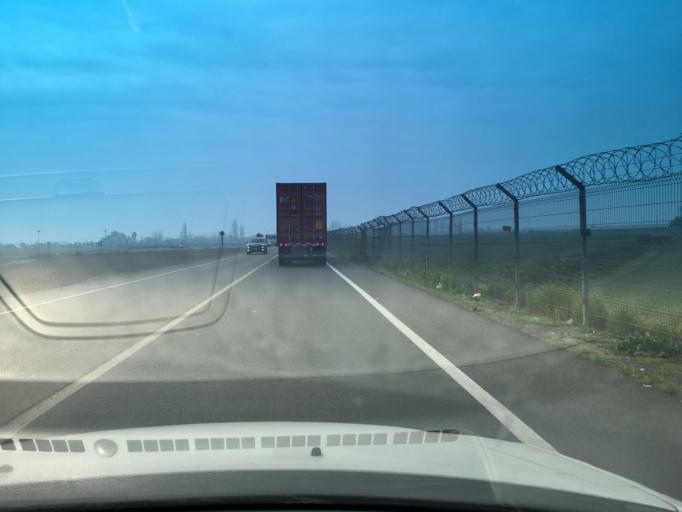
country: CL
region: Santiago Metropolitan
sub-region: Provincia de Chacabuco
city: Lampa
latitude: -33.3666
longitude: -70.8032
